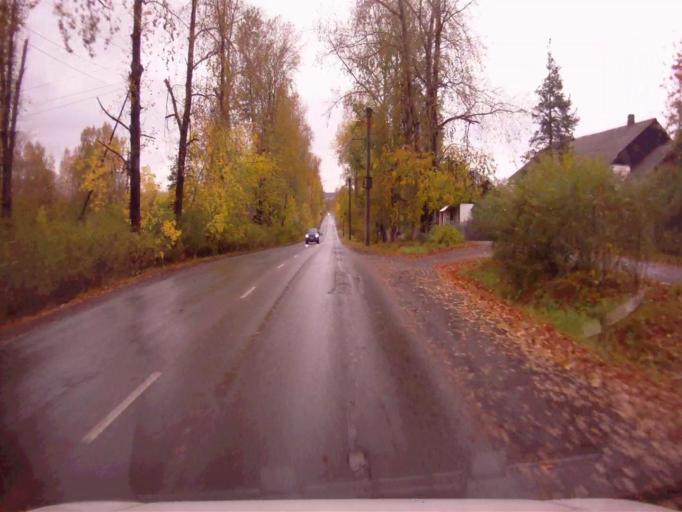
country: RU
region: Chelyabinsk
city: Verkhniy Ufaley
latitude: 56.0380
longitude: 60.2559
